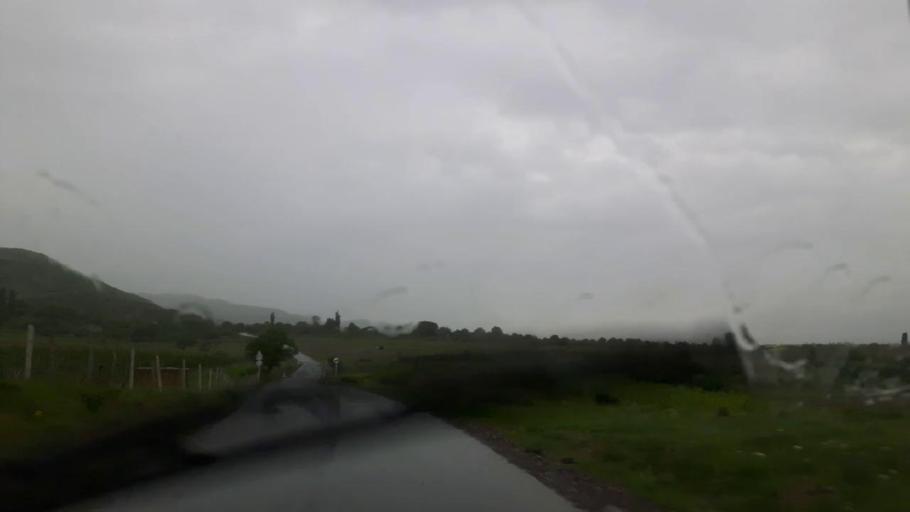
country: GE
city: Agara
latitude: 41.9823
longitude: 43.9495
